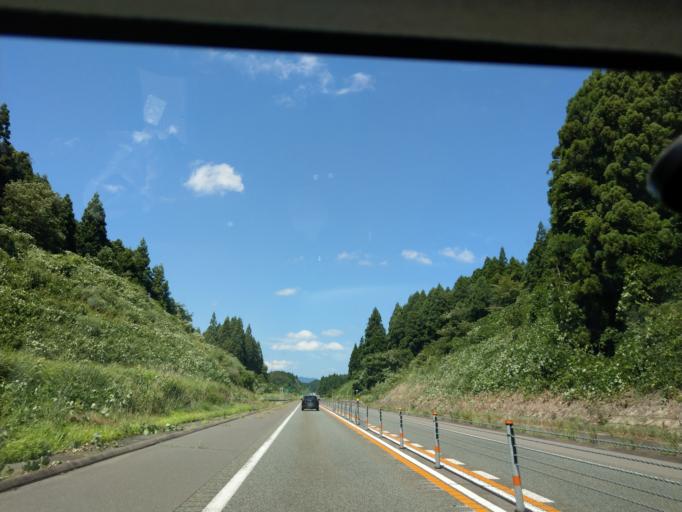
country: JP
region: Akita
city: Akita
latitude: 39.6893
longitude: 140.1857
